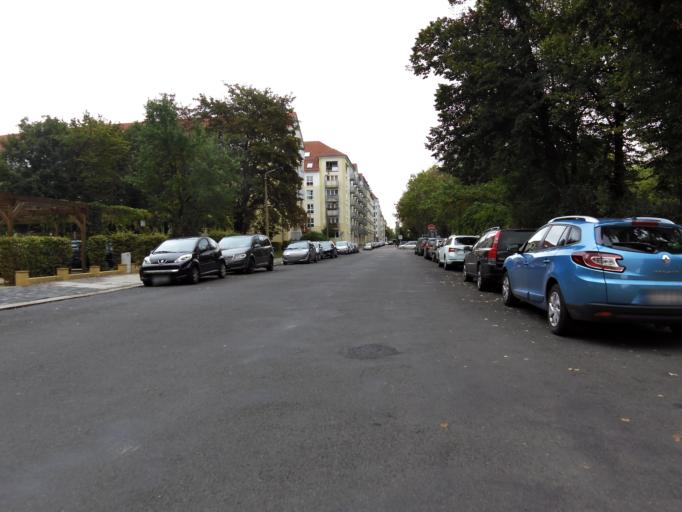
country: DE
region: Saxony
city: Leipzig
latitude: 51.3242
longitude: 12.3756
